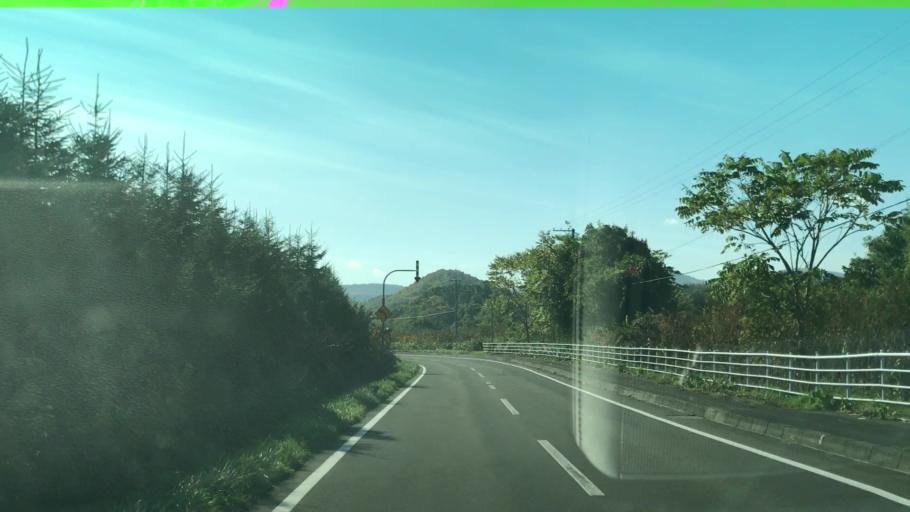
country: JP
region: Hokkaido
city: Yoichi
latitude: 43.1623
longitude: 140.8214
